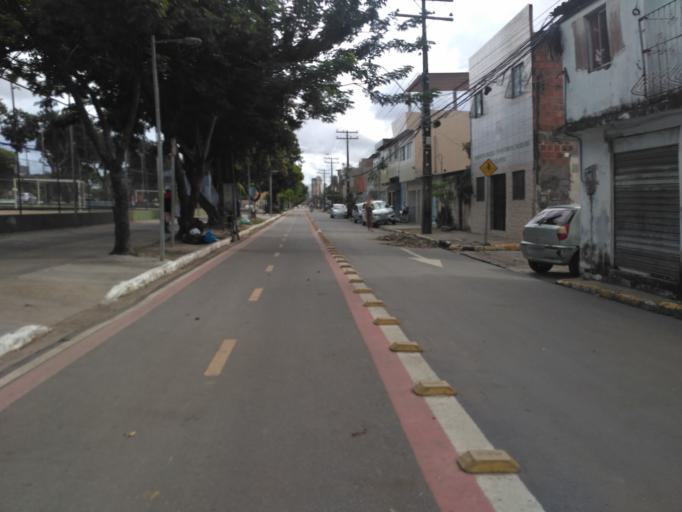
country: BR
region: Pernambuco
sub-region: Recife
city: Recife
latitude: -8.0375
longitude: -34.8752
